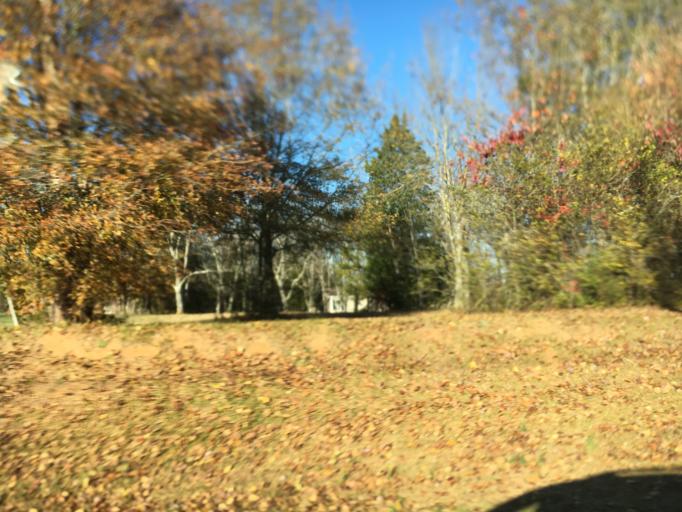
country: US
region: South Carolina
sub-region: Greenville County
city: Greer
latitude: 34.9641
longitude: -82.1898
